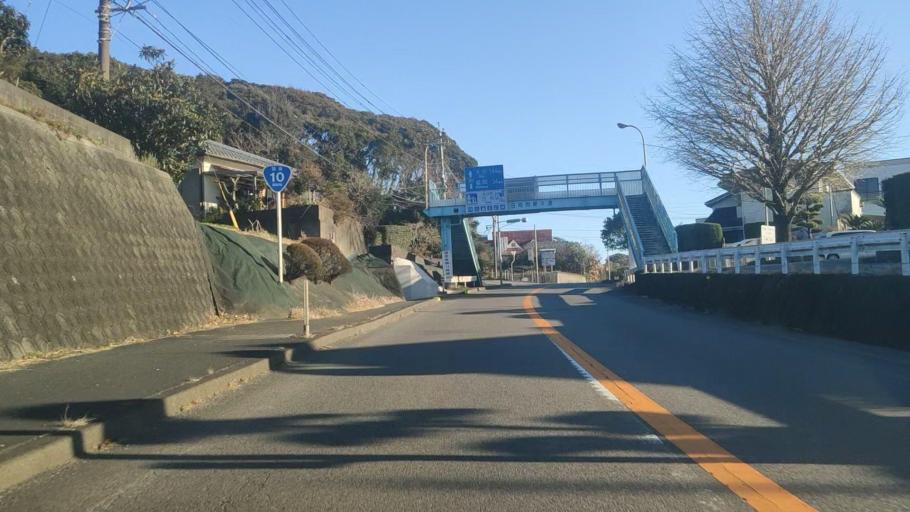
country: JP
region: Miyazaki
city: Takanabe
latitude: 32.3315
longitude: 131.6043
